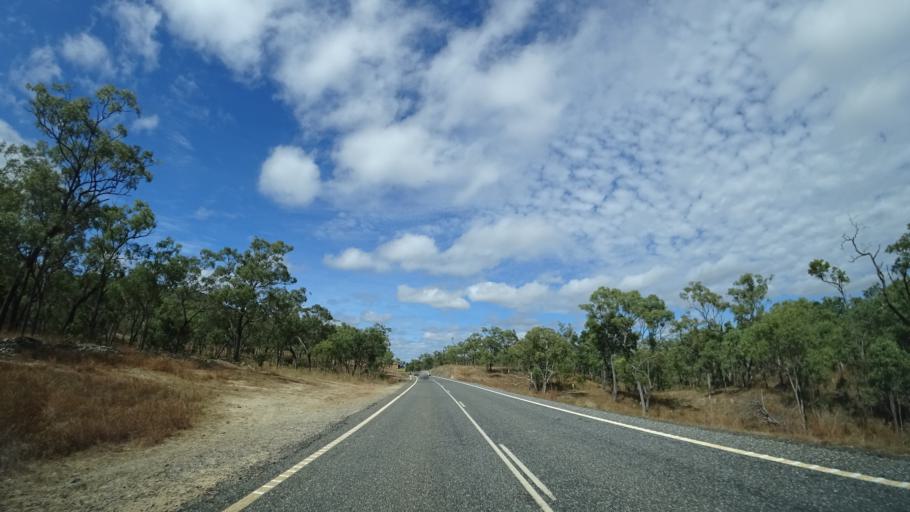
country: AU
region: Queensland
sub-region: Cairns
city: Port Douglas
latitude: -16.3312
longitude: 144.7218
